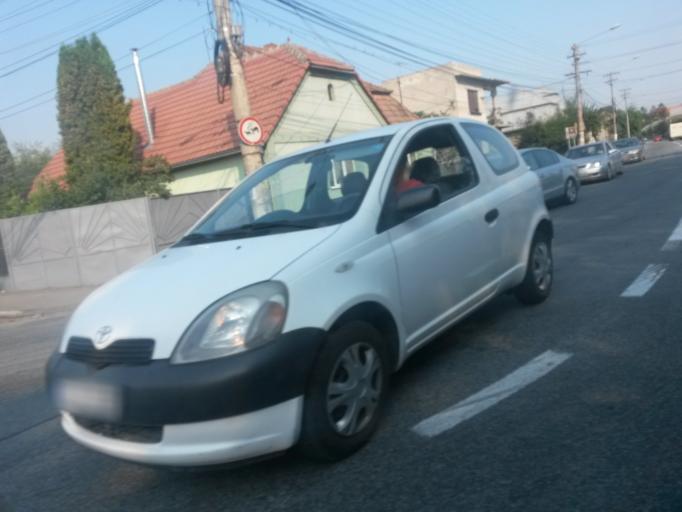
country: RO
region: Cluj
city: Turda
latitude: 46.5770
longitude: 23.7712
